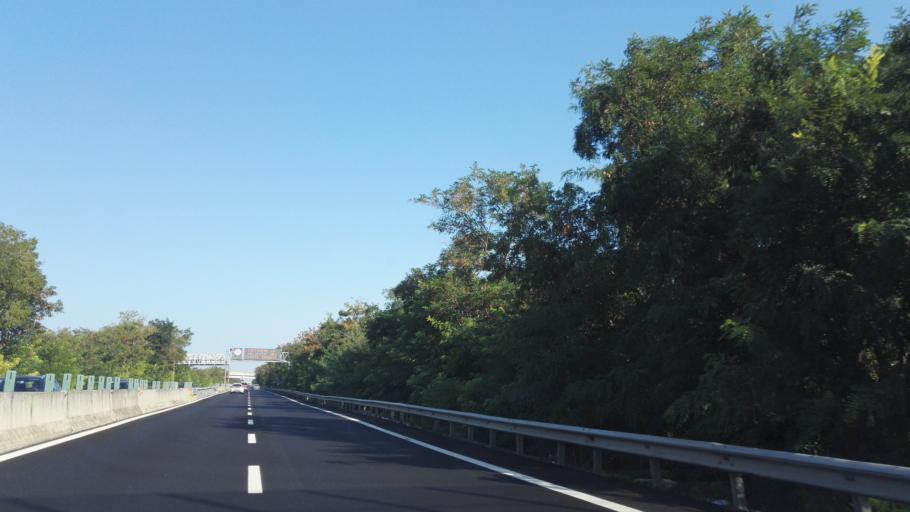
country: IT
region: Apulia
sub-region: Provincia di Bari
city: Mola di Bari
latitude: 41.0429
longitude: 17.1117
